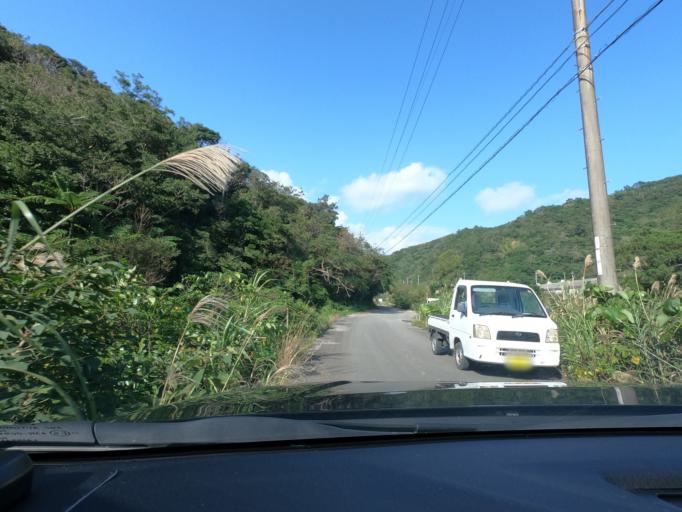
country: JP
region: Okinawa
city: Nago
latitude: 26.7653
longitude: 128.2110
